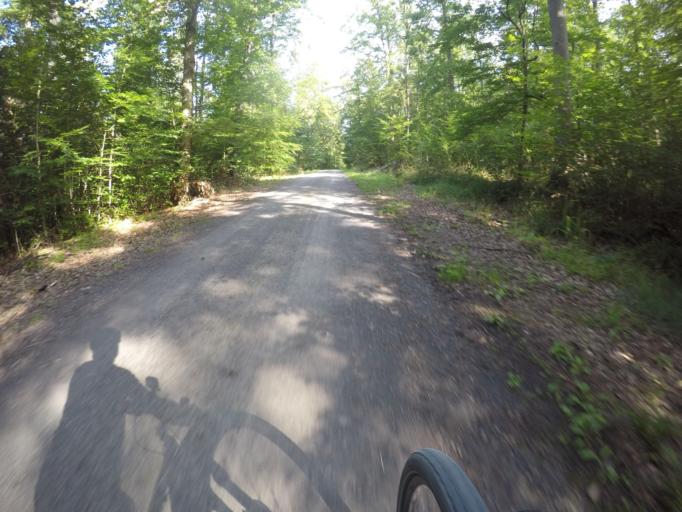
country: DE
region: Baden-Wuerttemberg
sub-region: Regierungsbezirk Stuttgart
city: Weissach
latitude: 48.8674
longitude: 8.9033
